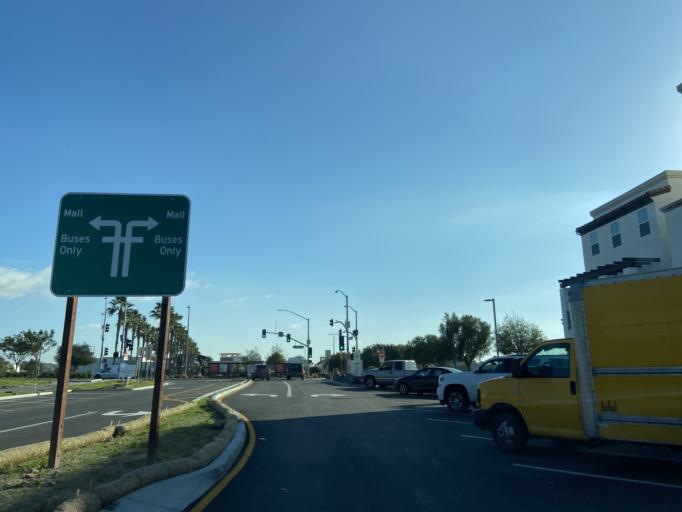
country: US
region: California
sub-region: San Diego County
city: Bonita
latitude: 32.6266
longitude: -116.9684
